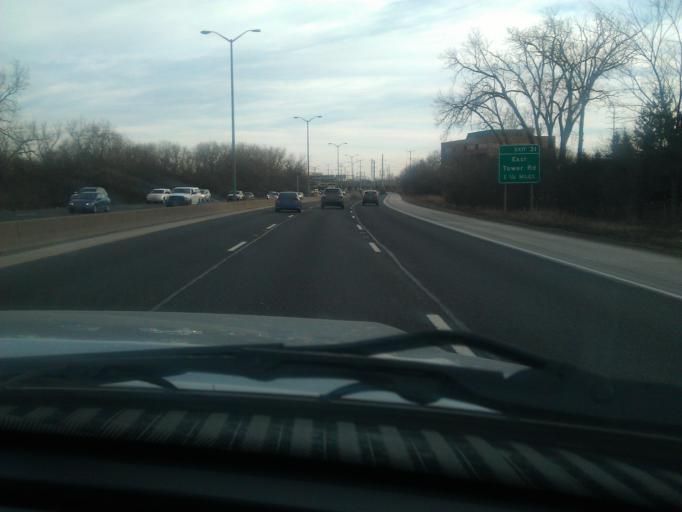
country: US
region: Illinois
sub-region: Cook County
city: Glencoe
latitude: 42.1329
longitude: -87.7856
